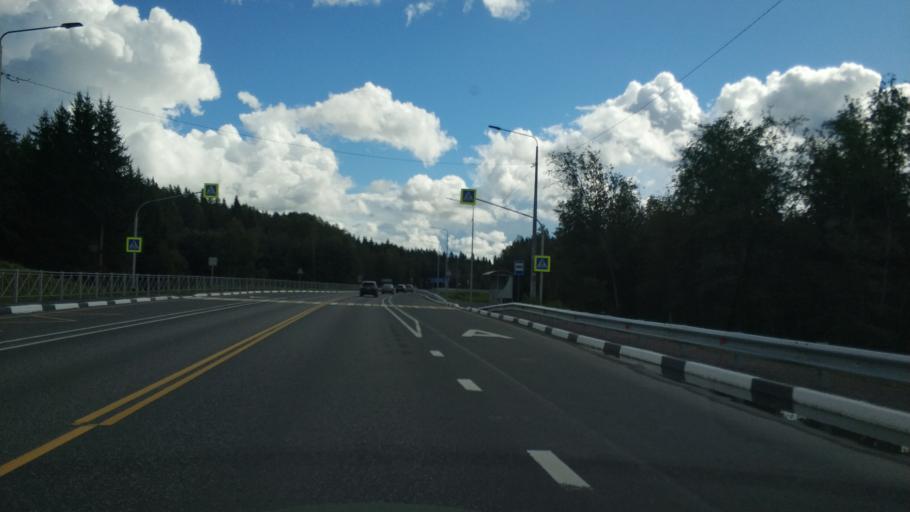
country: RU
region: Republic of Karelia
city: Ruskeala
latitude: 61.9170
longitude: 30.6229
